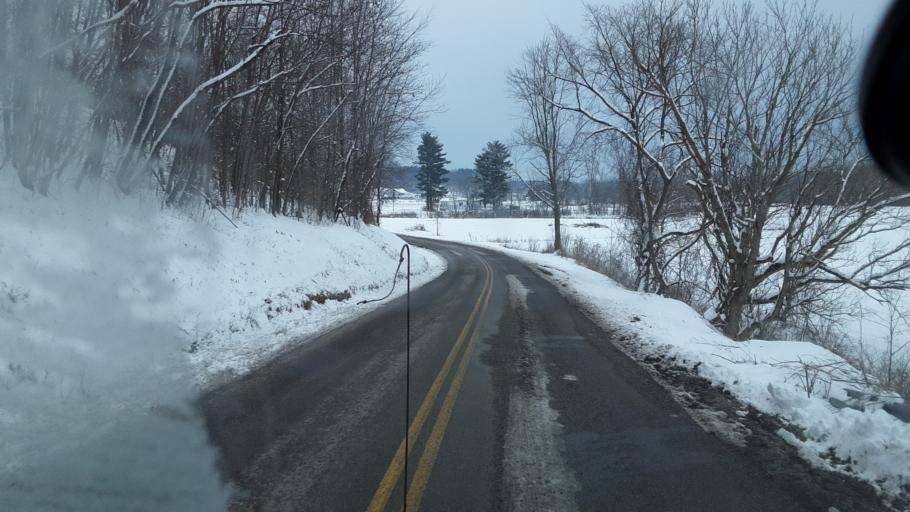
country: US
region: Ohio
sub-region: Perry County
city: Somerset
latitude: 39.8892
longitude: -82.2241
